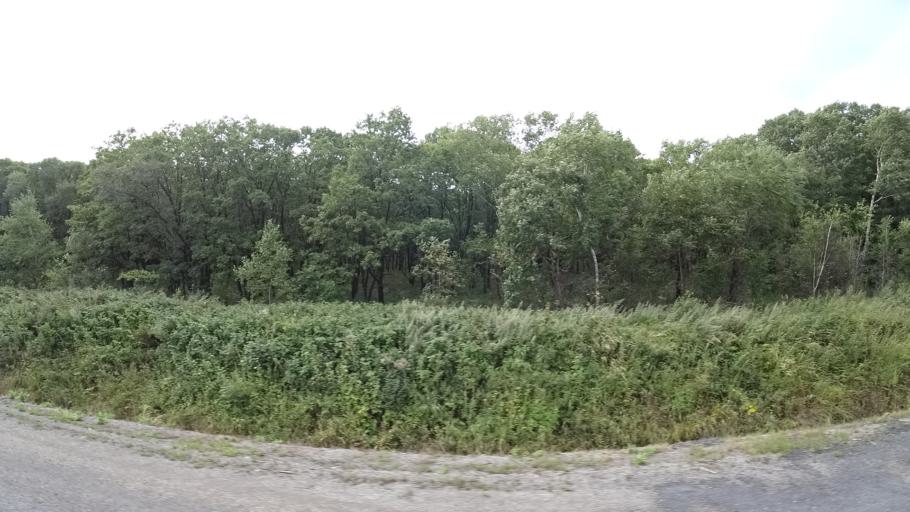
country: RU
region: Primorskiy
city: Lyalichi
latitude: 44.1033
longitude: 132.4236
